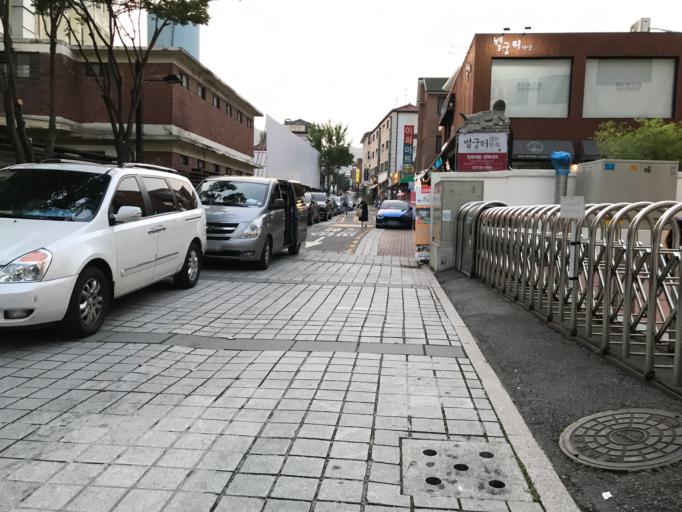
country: KR
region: Seoul
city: Seoul
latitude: 37.5763
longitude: 126.9842
